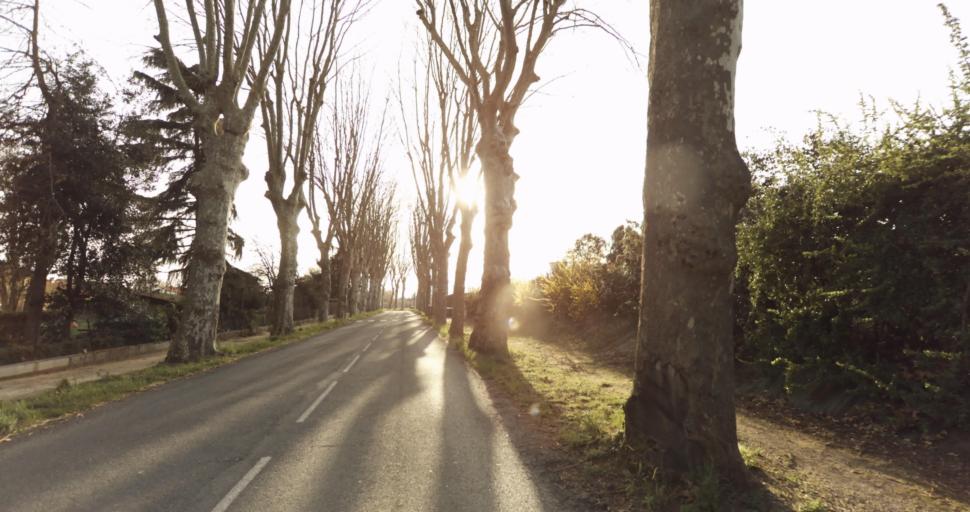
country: FR
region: Midi-Pyrenees
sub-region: Departement du Tarn
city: Saint-Sulpice-la-Pointe
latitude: 43.7771
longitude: 1.6734
